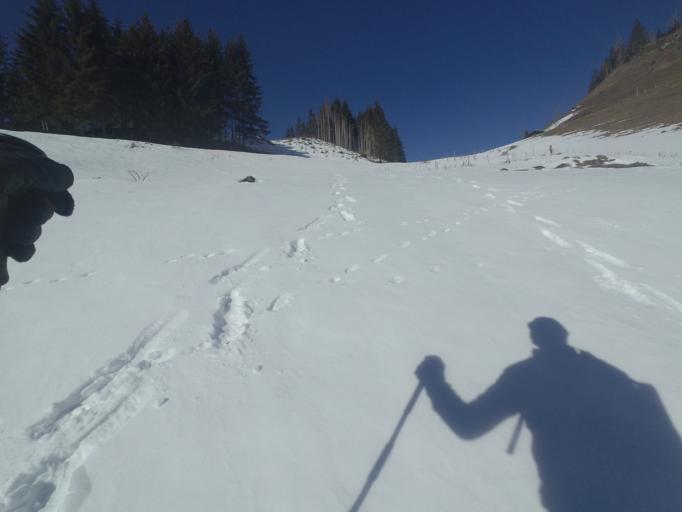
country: AT
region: Salzburg
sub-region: Politischer Bezirk Zell am See
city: Lend
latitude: 47.3198
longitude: 13.0396
